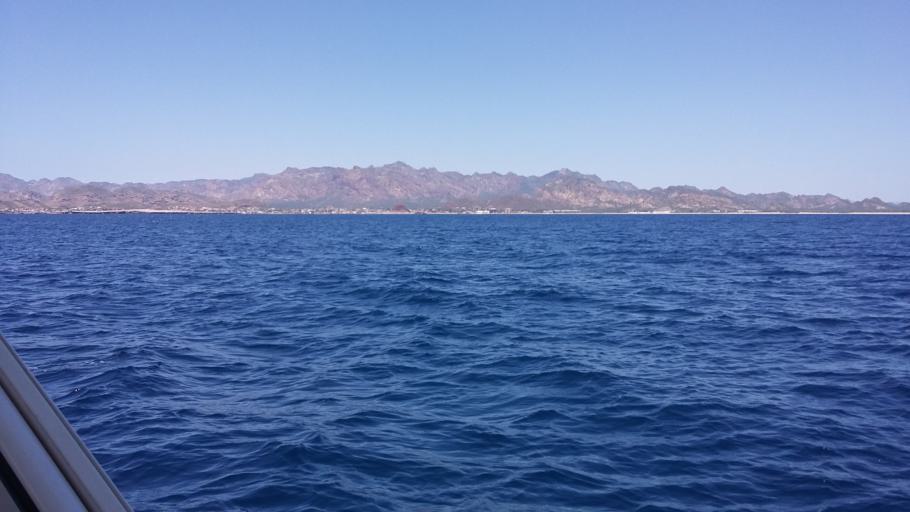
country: MX
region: Sonora
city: Heroica Guaymas
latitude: 27.9272
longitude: -111.0065
